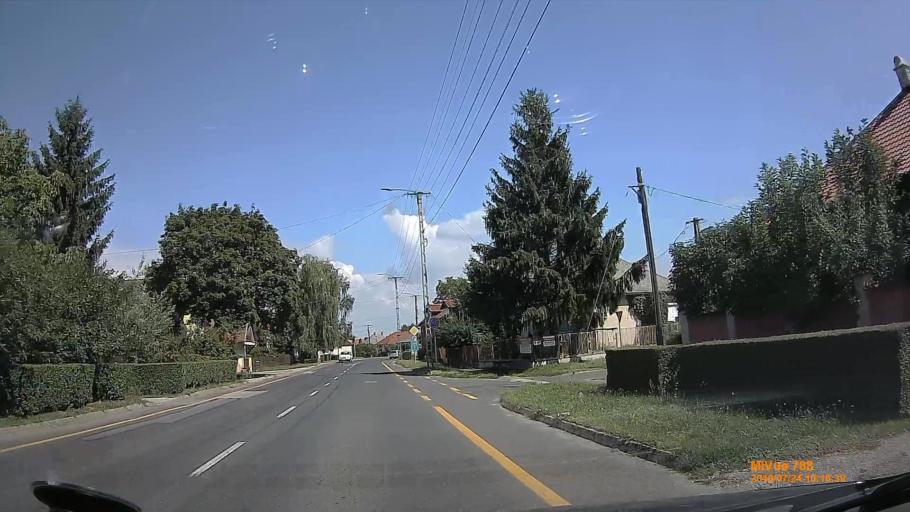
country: HU
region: Szabolcs-Szatmar-Bereg
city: Vasarosnameny
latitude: 48.1203
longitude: 22.3146
